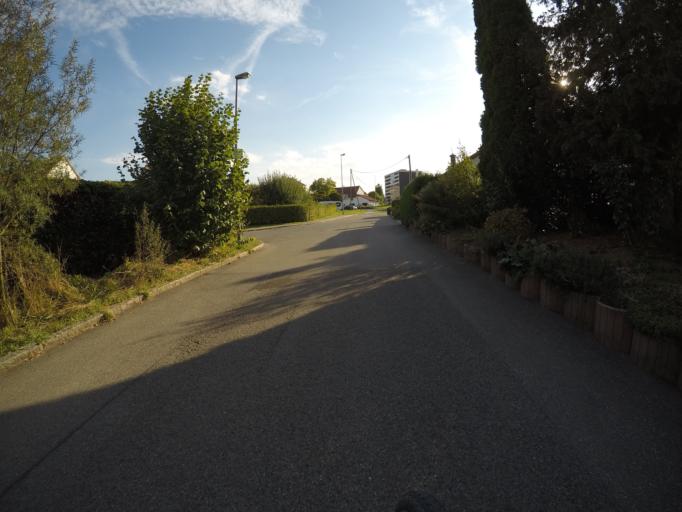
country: DE
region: Baden-Wuerttemberg
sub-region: Tuebingen Region
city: Pliezhausen
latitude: 48.5514
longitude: 9.2015
